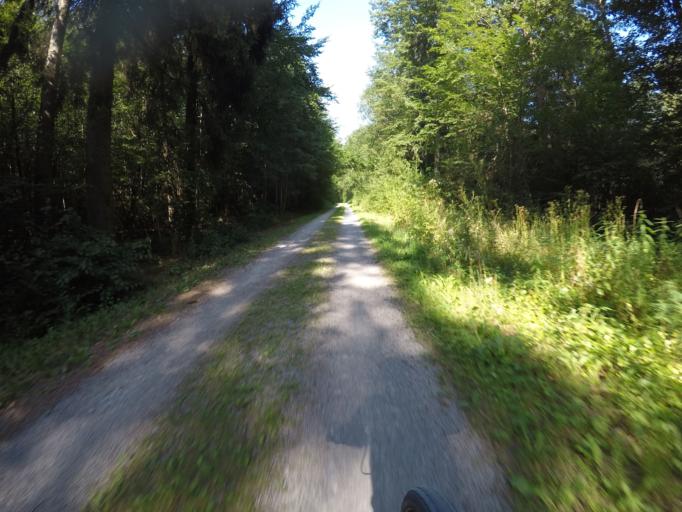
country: DE
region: Baden-Wuerttemberg
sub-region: Regierungsbezirk Stuttgart
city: Hildrizhausen
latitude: 48.6477
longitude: 8.9695
